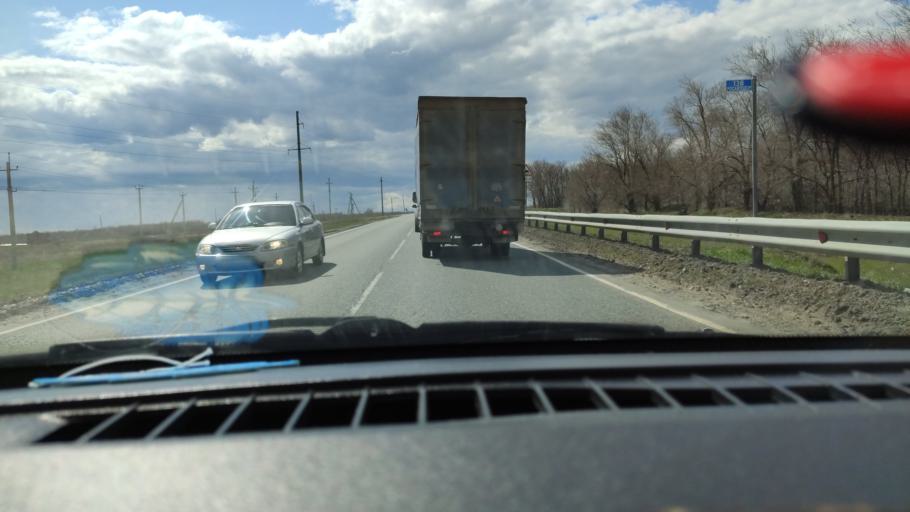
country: RU
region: Saratov
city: Balakovo
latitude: 52.1143
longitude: 47.7504
